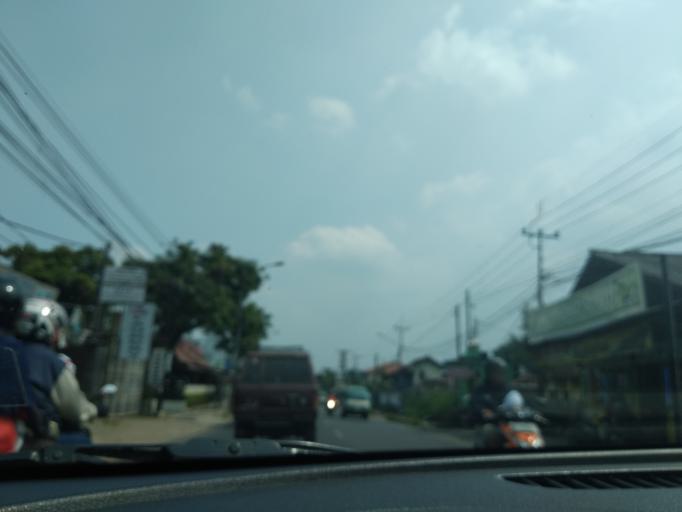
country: ID
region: West Java
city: Cimahi
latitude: -6.8636
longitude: 107.5080
